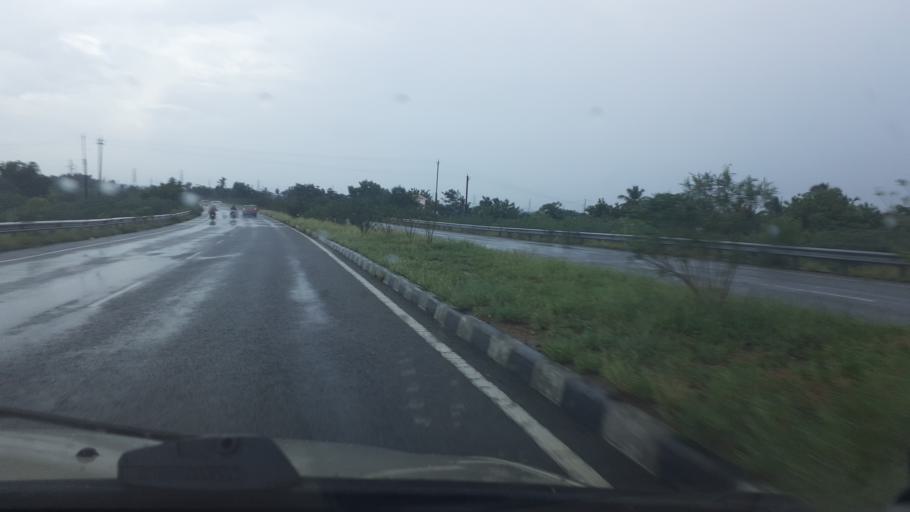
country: IN
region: Tamil Nadu
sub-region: Thoothukkudi
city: Kayattar
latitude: 8.9564
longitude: 77.7692
